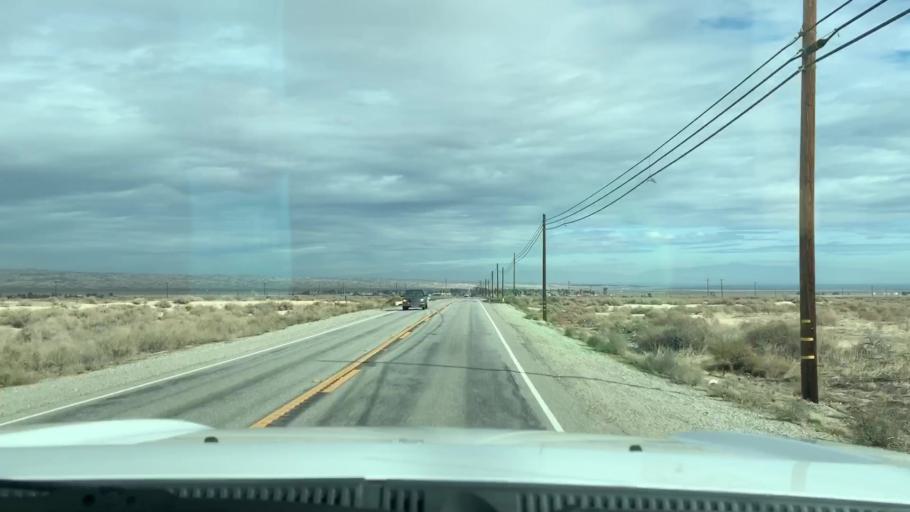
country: US
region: California
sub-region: Kern County
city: Ford City
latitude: 35.1905
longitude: -119.4336
